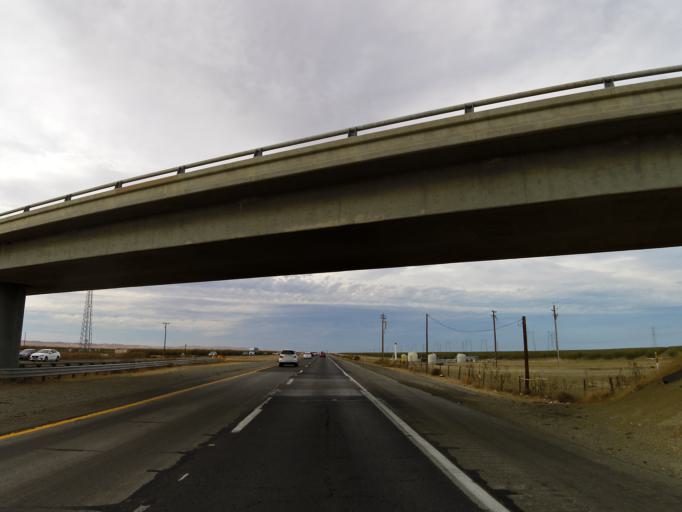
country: US
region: California
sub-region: Kings County
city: Kettleman City
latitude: 35.8751
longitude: -119.8520
